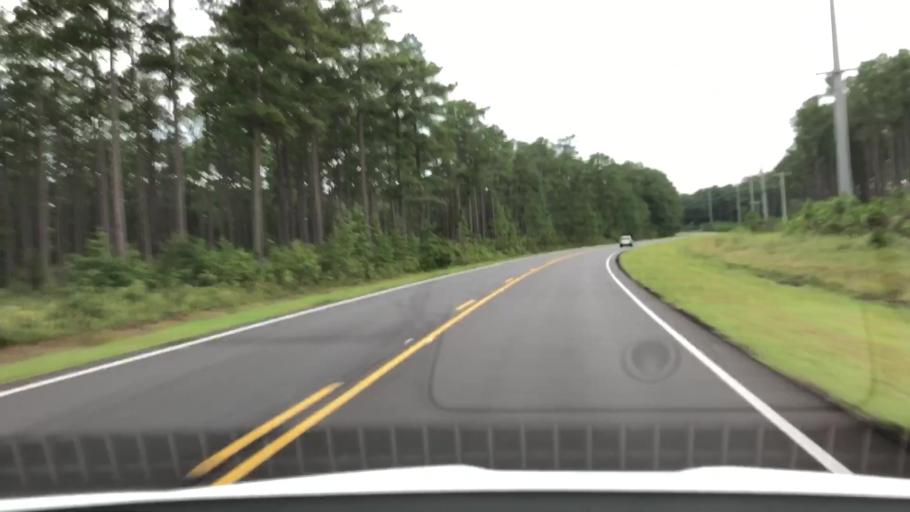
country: US
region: North Carolina
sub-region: Jones County
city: Maysville
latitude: 34.8178
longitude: -77.1460
